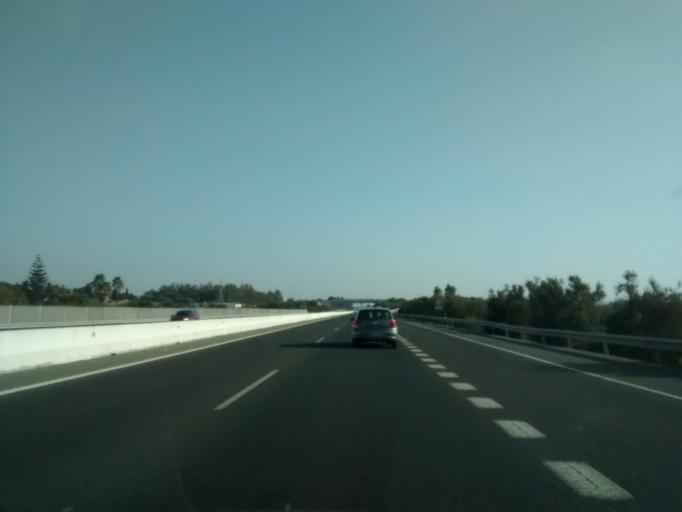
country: ES
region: Andalusia
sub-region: Provincia de Cadiz
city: Puerto Real
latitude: 36.5000
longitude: -6.1444
